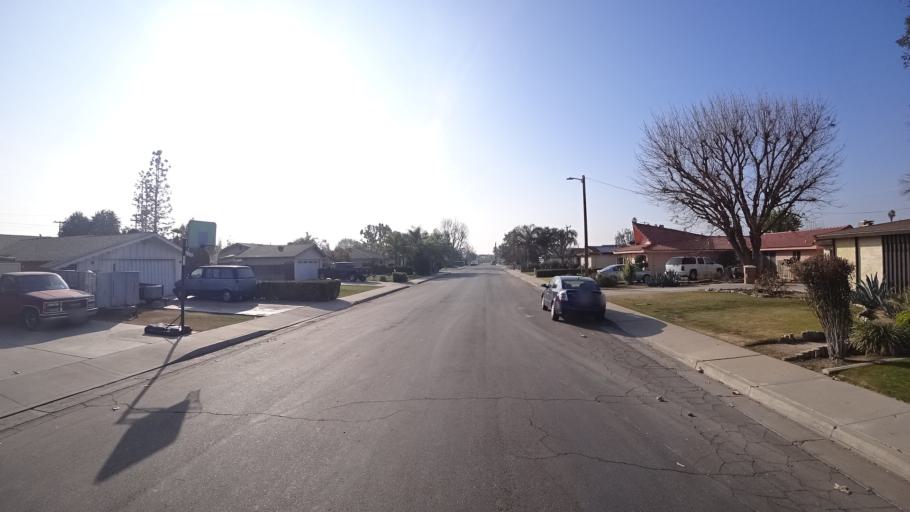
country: US
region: California
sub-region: Kern County
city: Bakersfield
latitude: 35.3297
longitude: -119.0322
